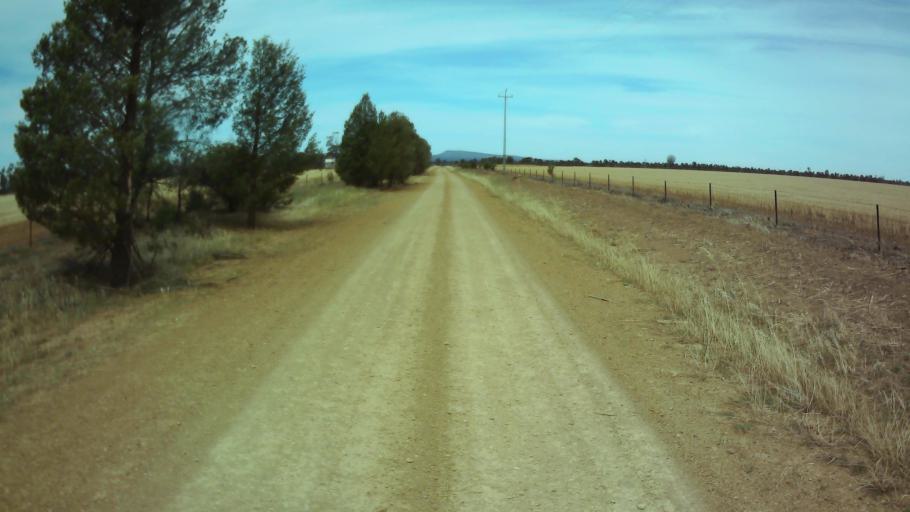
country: AU
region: New South Wales
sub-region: Weddin
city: Grenfell
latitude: -33.9418
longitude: 147.7814
